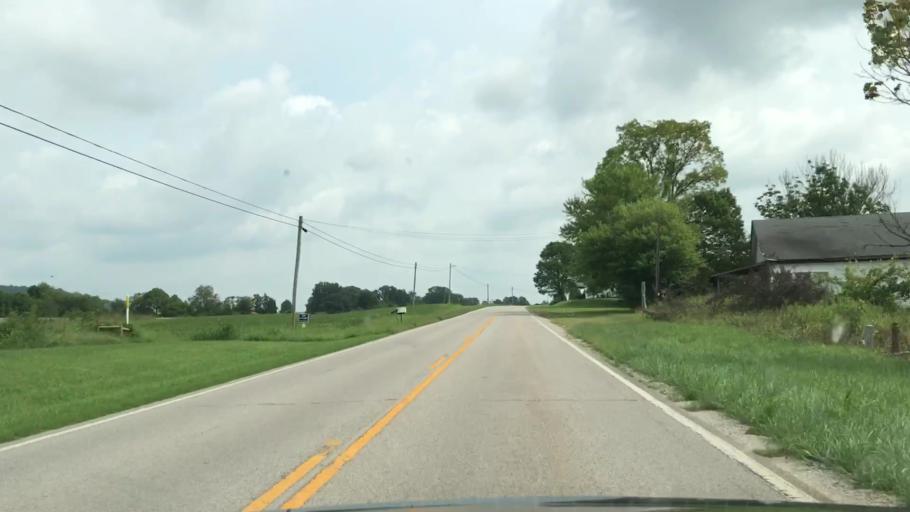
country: US
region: Kentucky
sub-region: Barren County
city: Cave City
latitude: 37.1061
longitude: -85.9997
